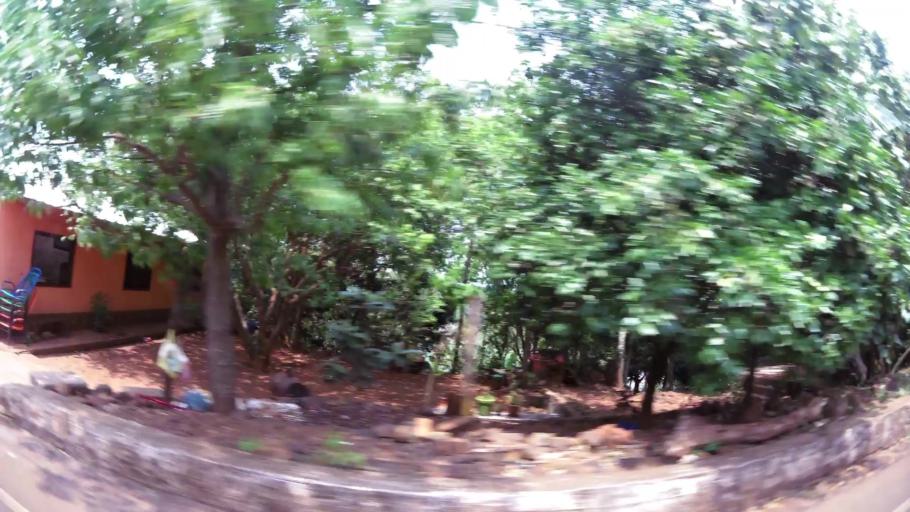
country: AR
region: Misiones
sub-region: Departamento de Iguazu
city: Puerto Iguazu
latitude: -25.5953
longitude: -54.5978
